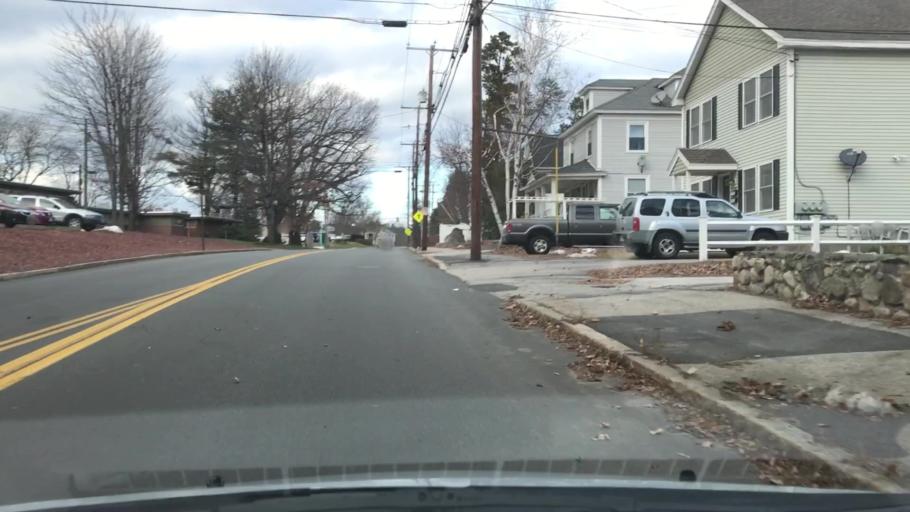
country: US
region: New Hampshire
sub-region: Hillsborough County
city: Manchester
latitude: 42.9833
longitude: -71.4348
